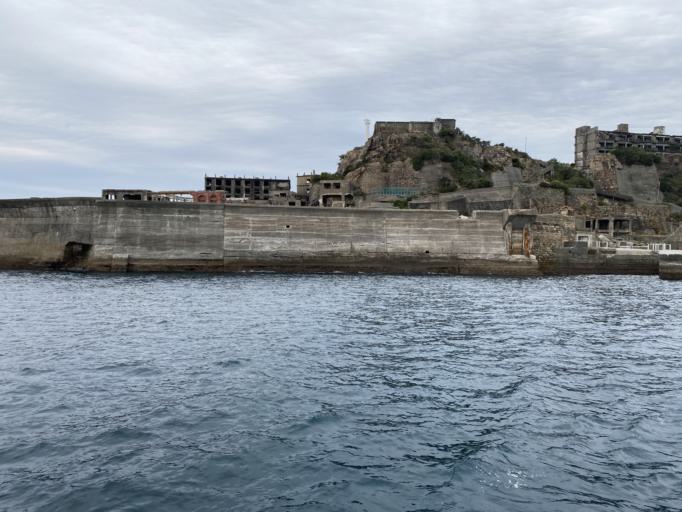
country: JP
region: Nagasaki
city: Nagasaki-shi
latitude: 32.6258
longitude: 129.7389
